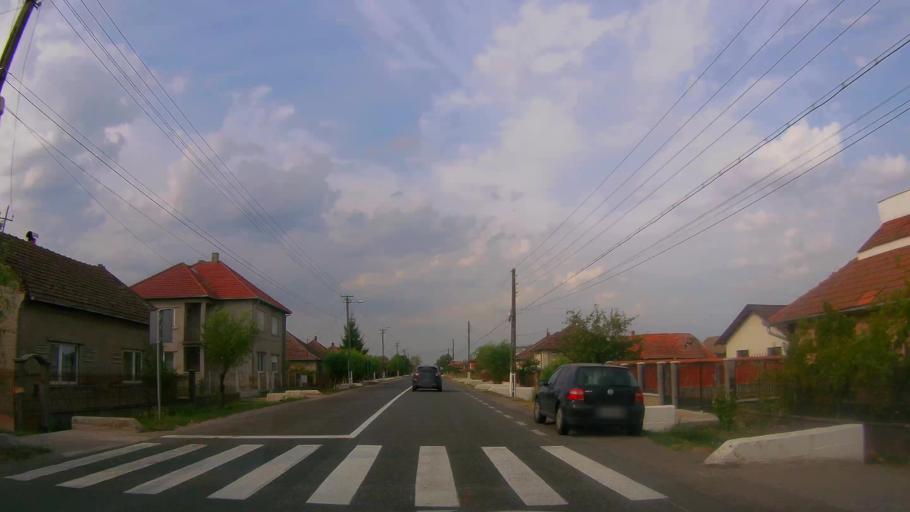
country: RO
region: Satu Mare
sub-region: Oras Ardud
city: Ardud
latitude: 47.6291
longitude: 22.8787
